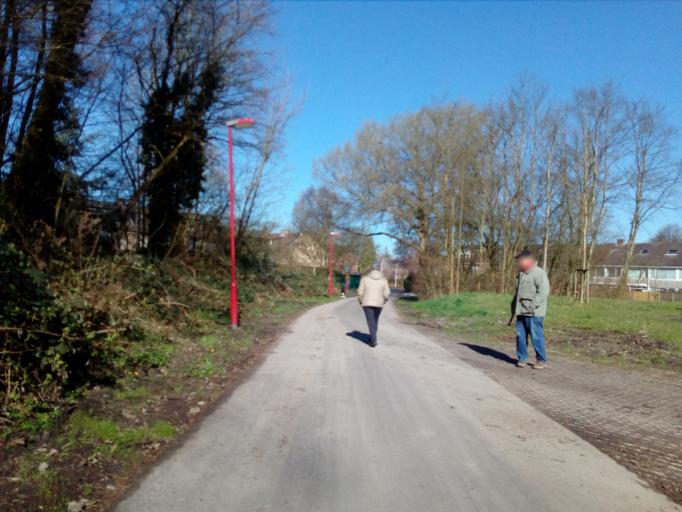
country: NL
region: South Holland
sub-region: Gemeente Zoetermeer
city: Zoetermeer
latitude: 52.0503
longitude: 4.4668
